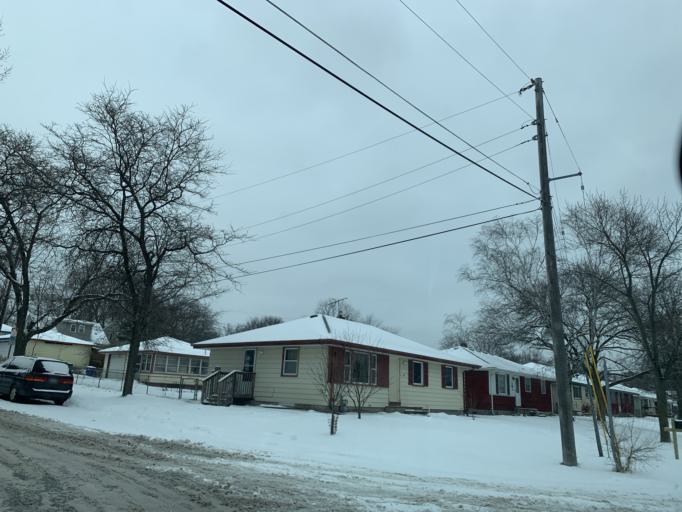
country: US
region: Minnesota
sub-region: Ramsey County
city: Little Canada
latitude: 44.9873
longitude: -93.1038
